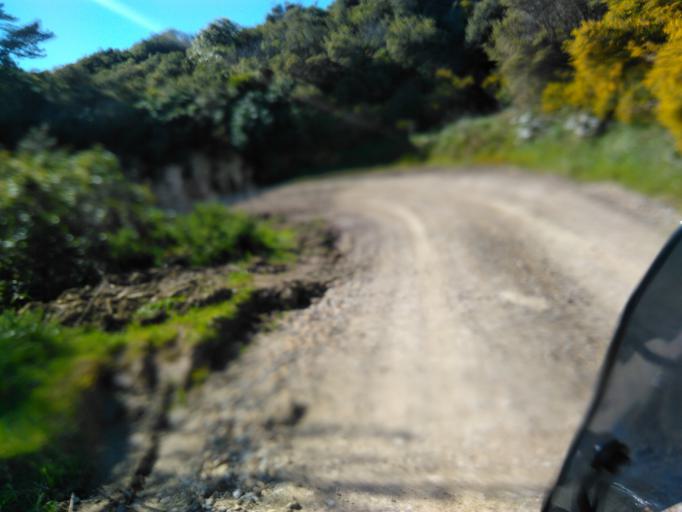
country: NZ
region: Gisborne
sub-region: Gisborne District
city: Gisborne
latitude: -38.3964
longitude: 177.6666
